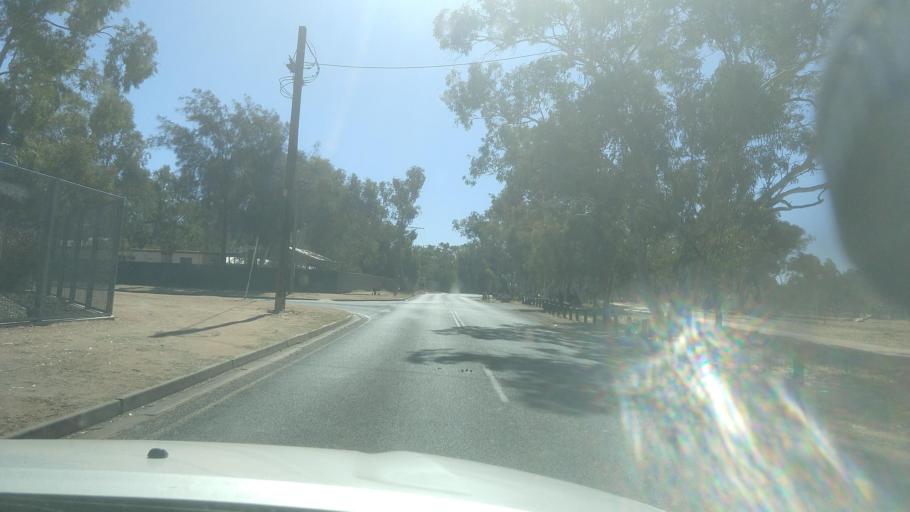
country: AU
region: Northern Territory
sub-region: Alice Springs
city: Alice Springs
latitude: -23.7188
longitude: 133.8741
